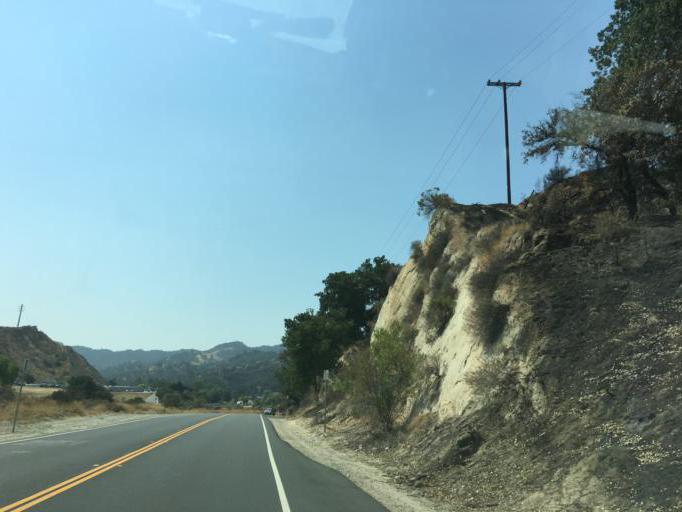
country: US
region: California
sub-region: Los Angeles County
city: Santa Clarita
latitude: 34.3647
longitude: -118.5571
